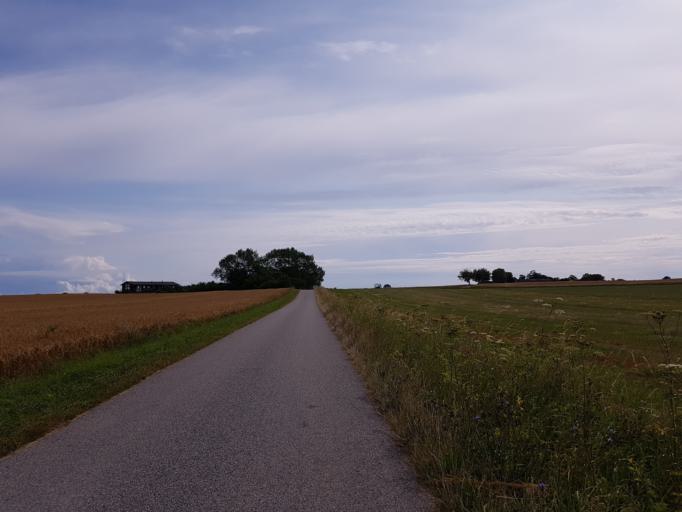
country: DK
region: Zealand
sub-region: Guldborgsund Kommune
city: Nykobing Falster
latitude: 54.5760
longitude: 11.9692
